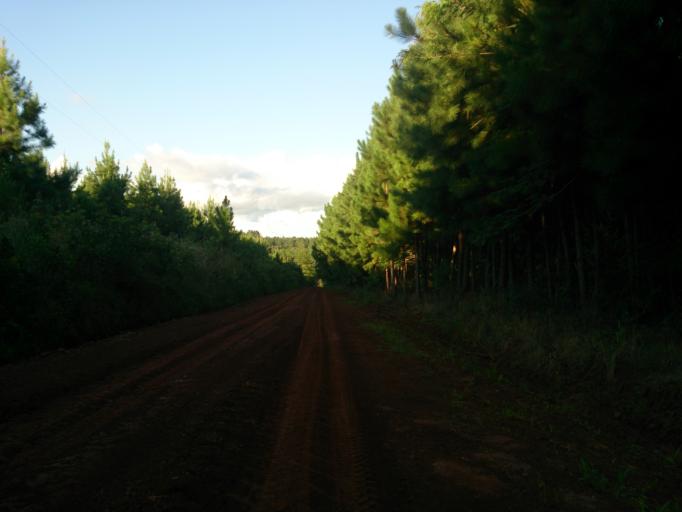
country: AR
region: Misiones
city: Florentino Ameghino
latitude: -27.5683
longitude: -55.1684
